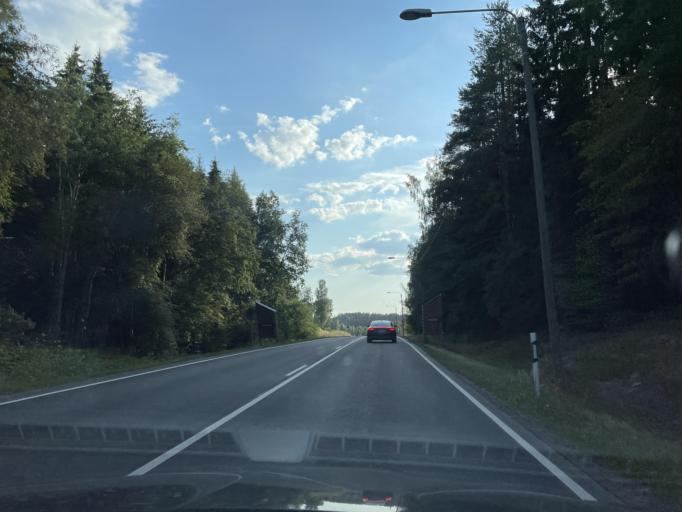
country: FI
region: Haeme
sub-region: Haemeenlinna
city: Tuulos
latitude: 61.1082
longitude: 24.8691
